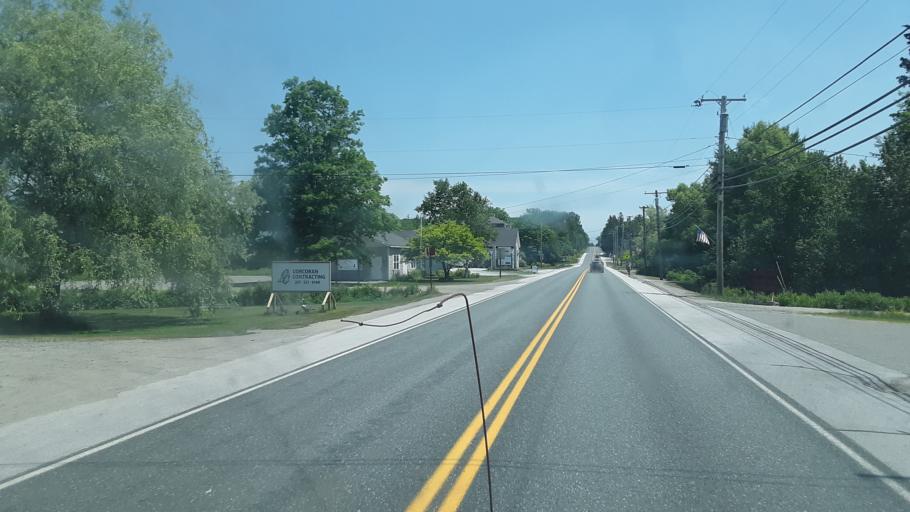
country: US
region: Maine
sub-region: Hancock County
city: Hancock
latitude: 44.5296
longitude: -68.2565
